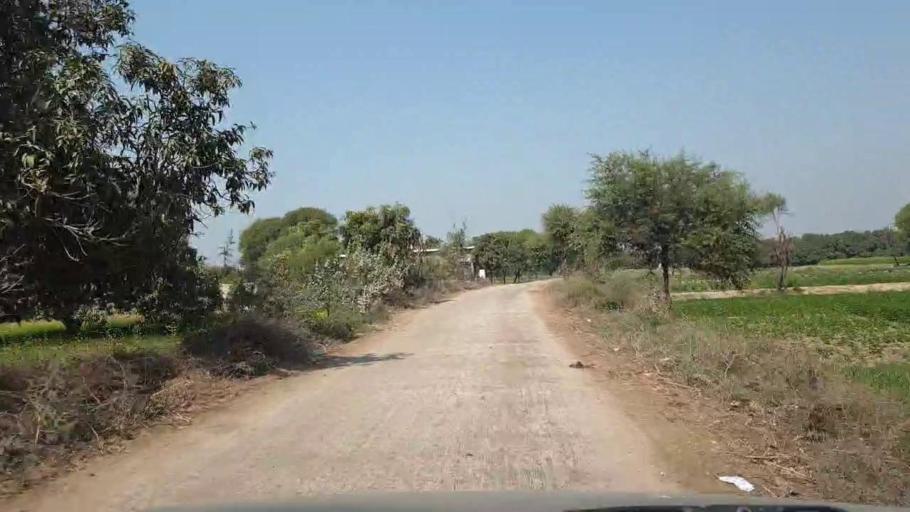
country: PK
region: Sindh
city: Tando Allahyar
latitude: 25.4286
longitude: 68.6539
